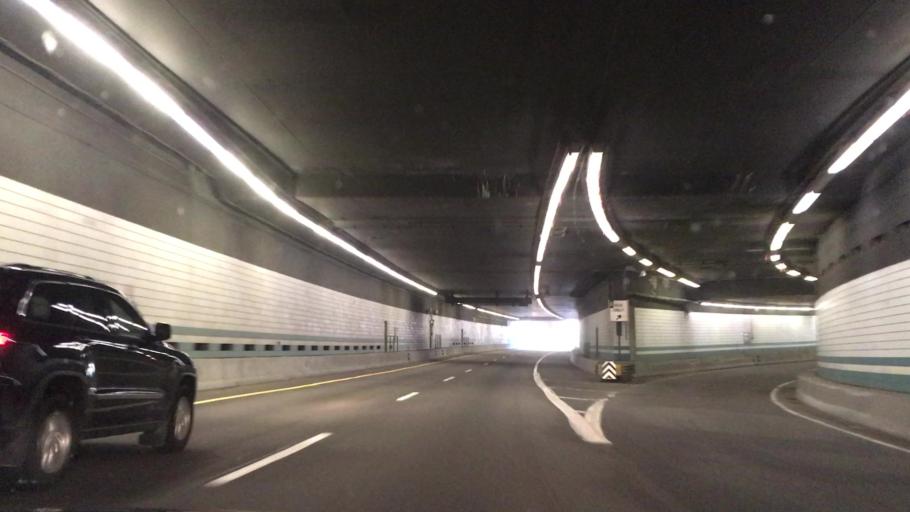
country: US
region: Massachusetts
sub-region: Suffolk County
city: Boston
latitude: 42.3497
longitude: -71.0551
